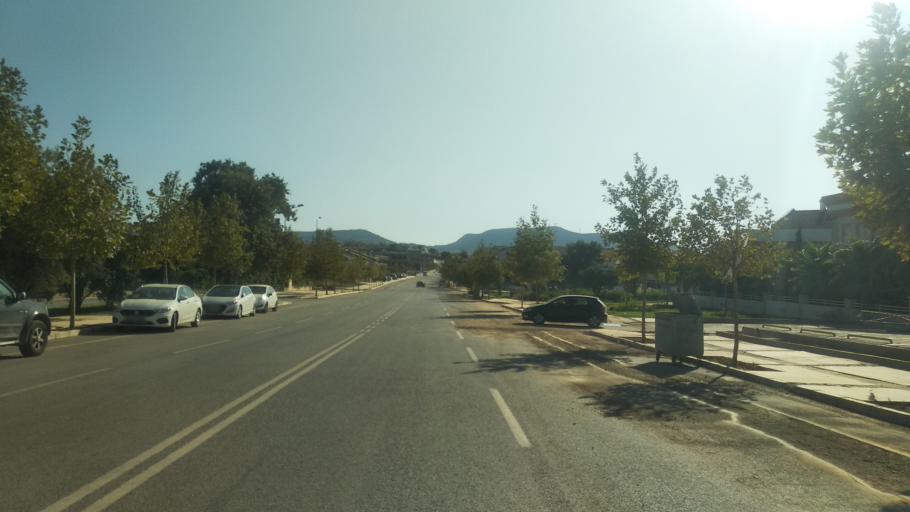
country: TR
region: Izmir
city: Urla
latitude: 38.3581
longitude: 26.8747
